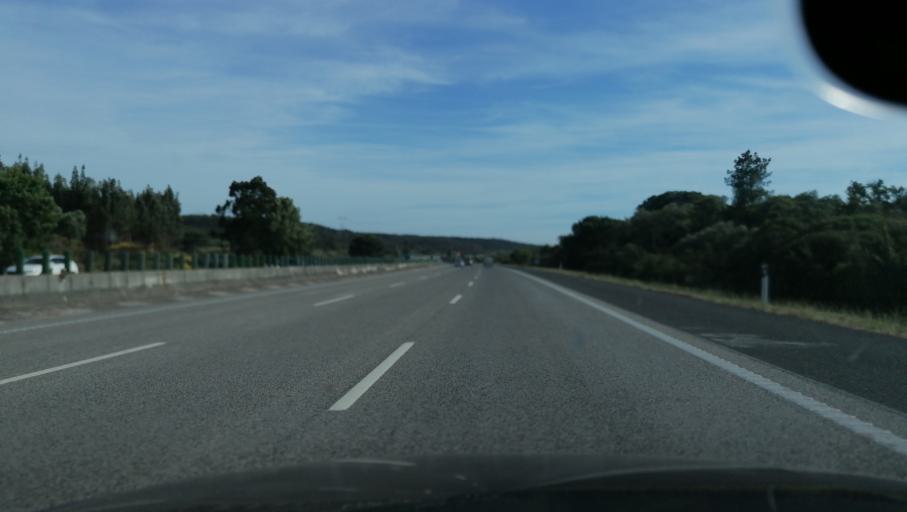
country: PT
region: Lisbon
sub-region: Azambuja
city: Azambuja
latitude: 39.0816
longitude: -8.9320
